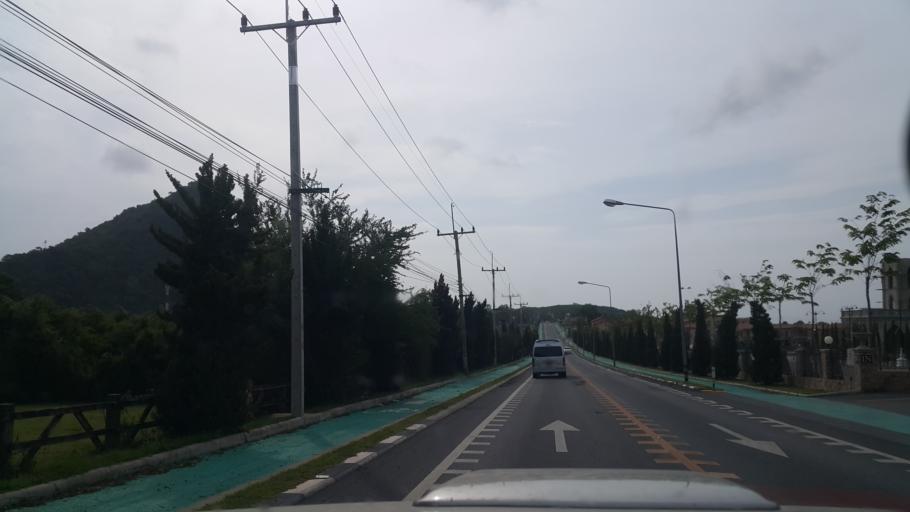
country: TH
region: Rayong
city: Ban Chang
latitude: 12.7611
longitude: 100.9640
